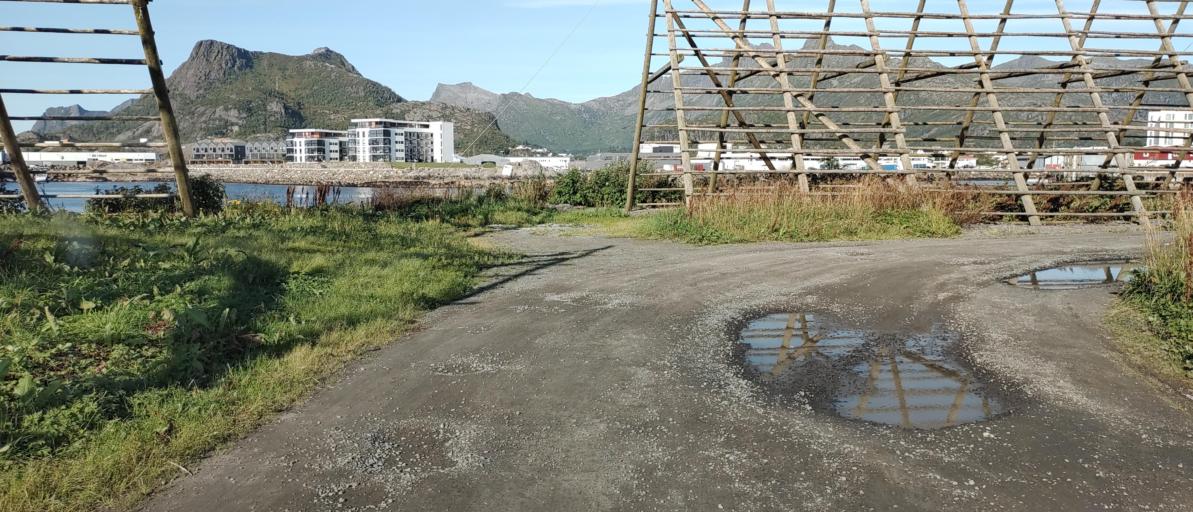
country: NO
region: Nordland
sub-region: Vagan
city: Svolvaer
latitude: 68.2268
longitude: 14.5689
